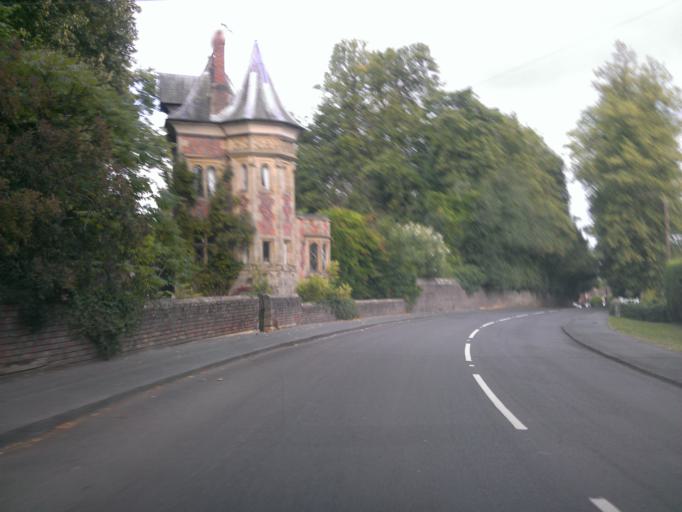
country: GB
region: England
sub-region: Kent
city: Tonbridge
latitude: 51.1966
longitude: 0.2080
